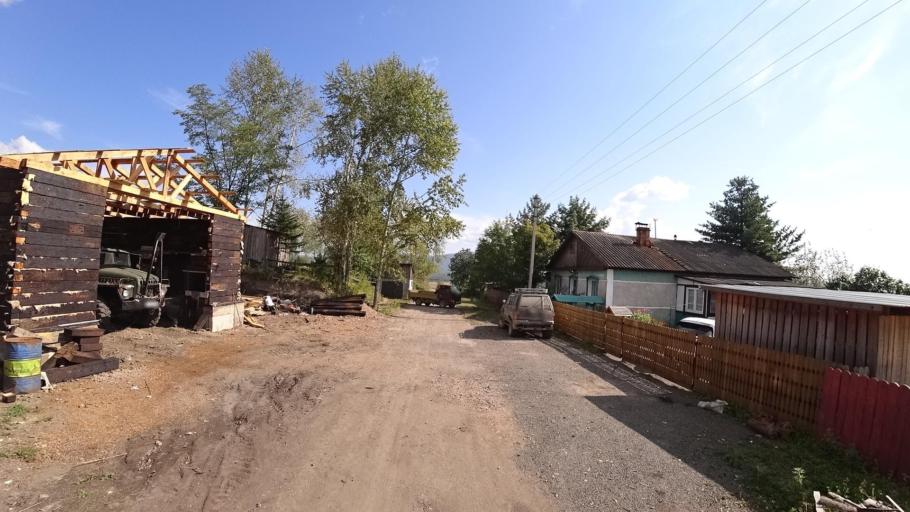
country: RU
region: Jewish Autonomous Oblast
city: Birakan
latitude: 49.0096
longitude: 131.7441
